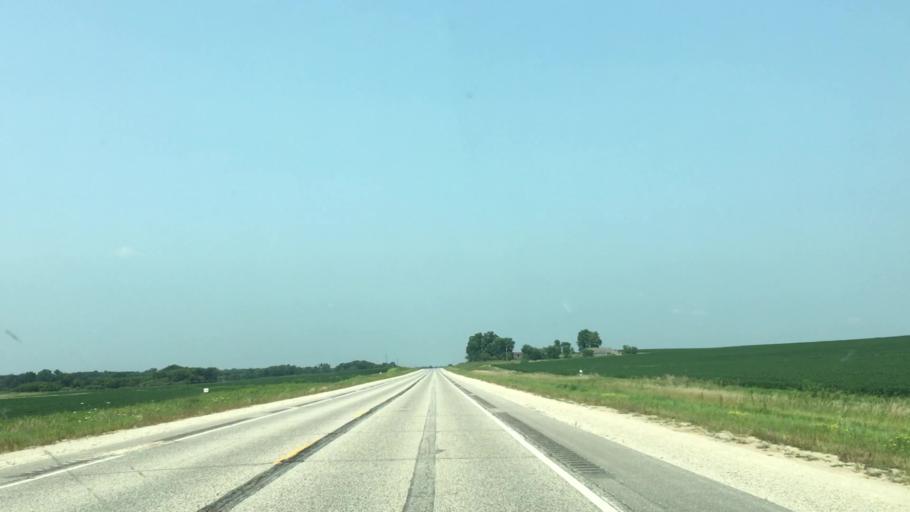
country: US
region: Iowa
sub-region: Fayette County
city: Fayette
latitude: 42.7903
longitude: -91.8049
